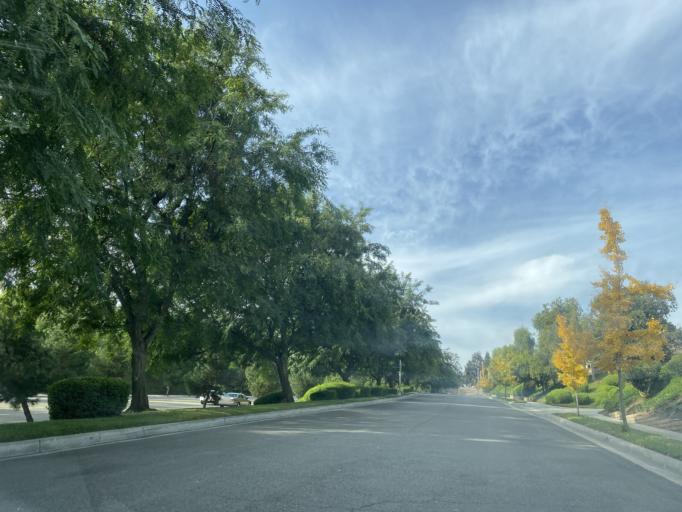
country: US
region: California
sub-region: Orange County
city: Brea
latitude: 33.8946
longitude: -117.8879
